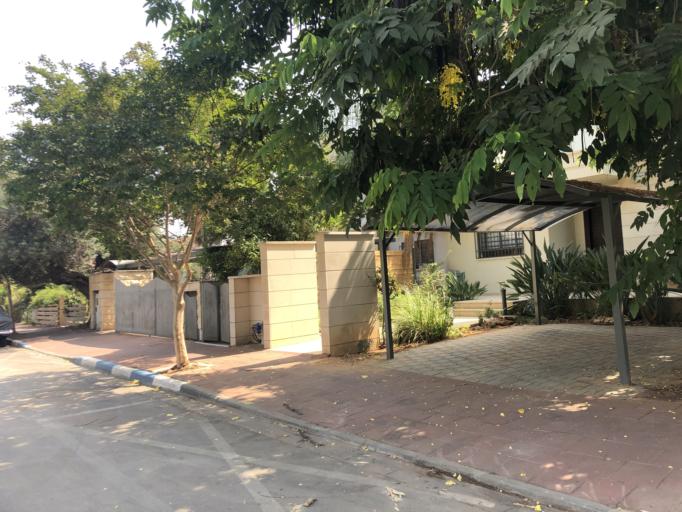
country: IL
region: Tel Aviv
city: Giv`atayim
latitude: 32.0572
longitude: 34.8305
